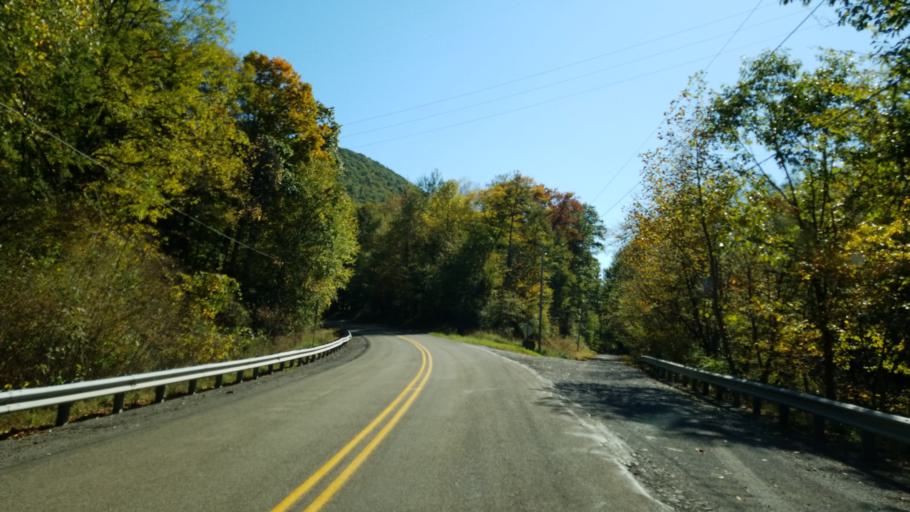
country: US
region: Pennsylvania
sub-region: Elk County
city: Saint Marys
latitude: 41.2696
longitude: -78.4032
